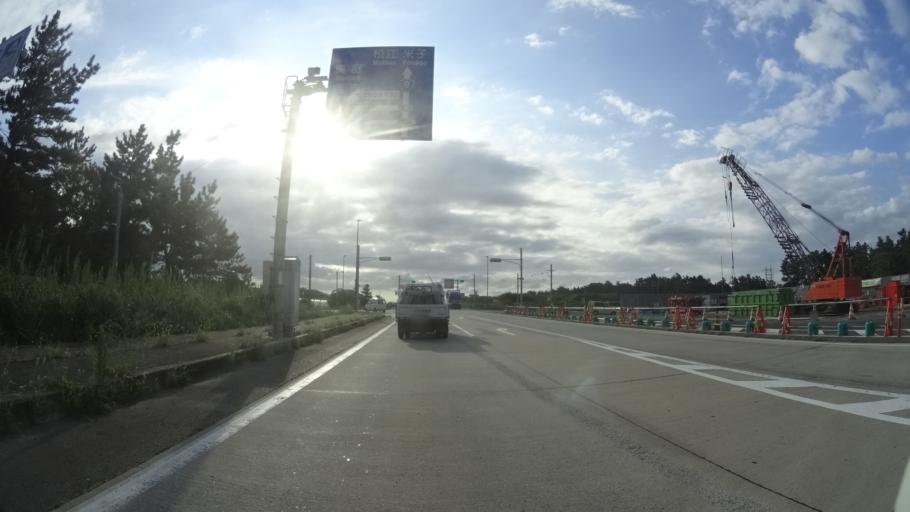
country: JP
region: Tottori
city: Kurayoshi
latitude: 35.4986
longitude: 133.8177
